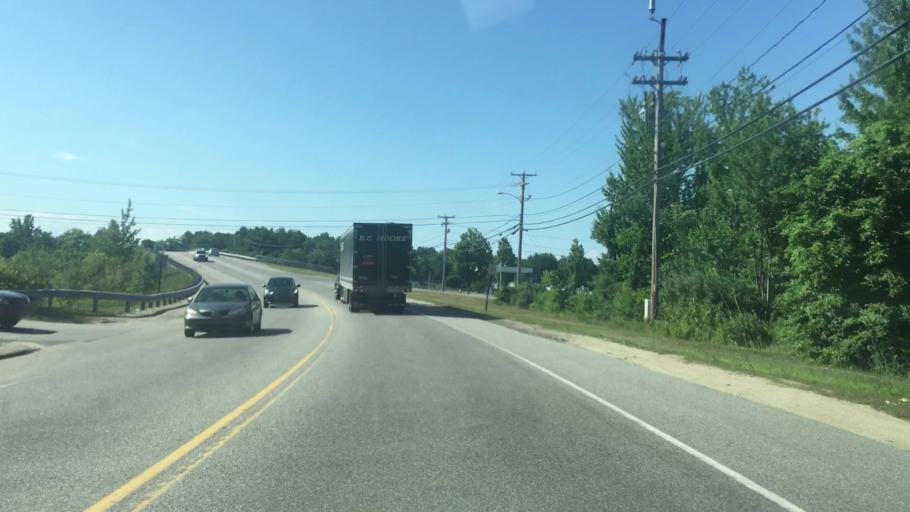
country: US
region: Maine
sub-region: York County
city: Saco
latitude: 43.5208
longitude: -70.4571
